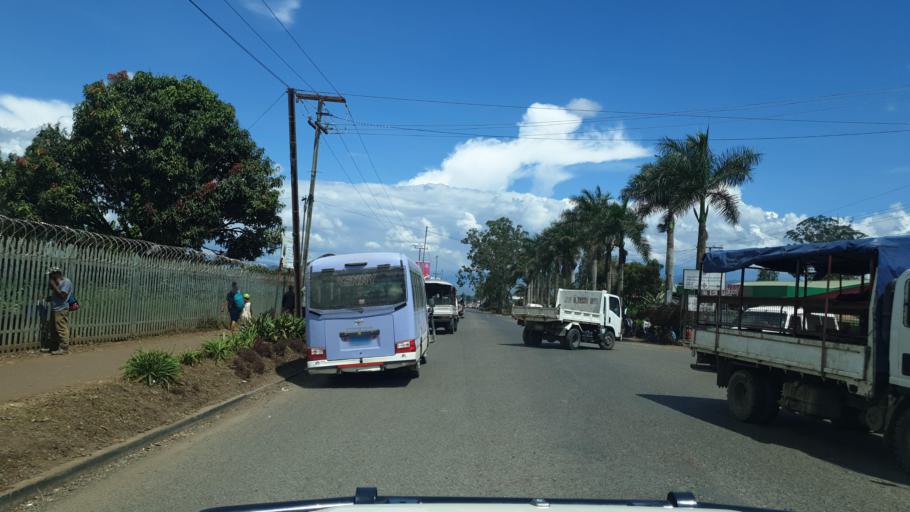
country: PG
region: Eastern Highlands
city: Goroka
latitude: -6.0770
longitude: 145.3893
